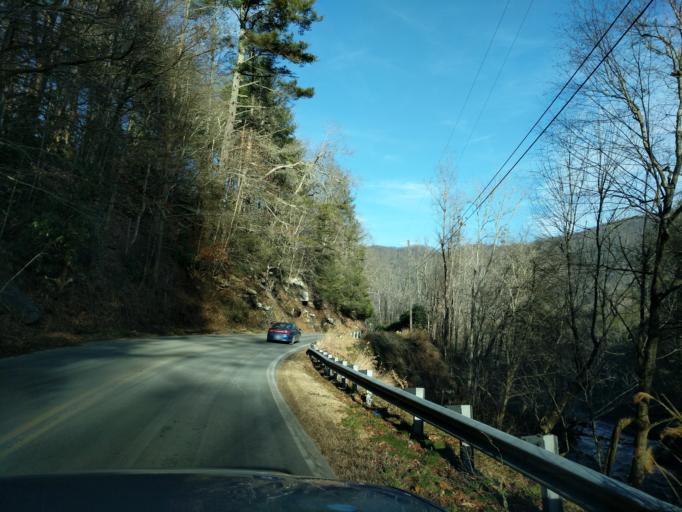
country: US
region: North Carolina
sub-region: Henderson County
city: Edneyville
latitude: 35.4356
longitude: -82.3017
